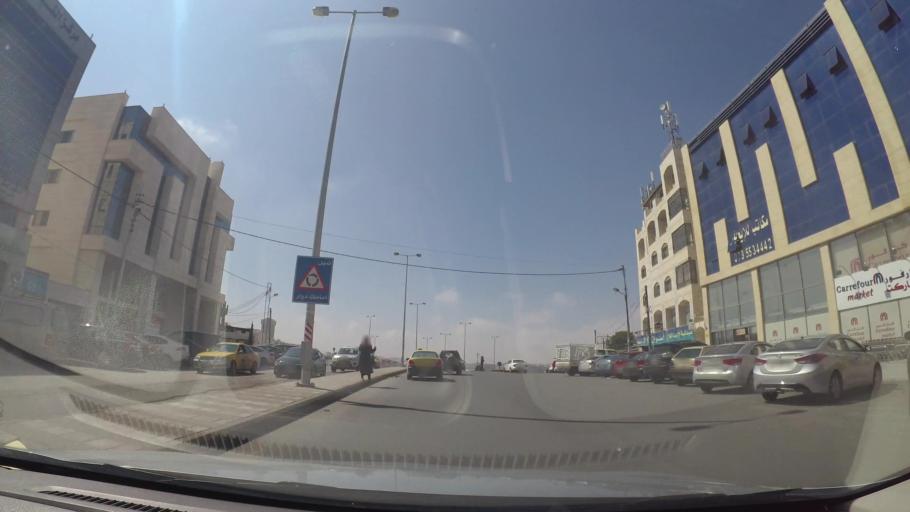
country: JO
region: Amman
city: Al Bunayyat ash Shamaliyah
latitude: 31.9151
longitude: 35.8879
